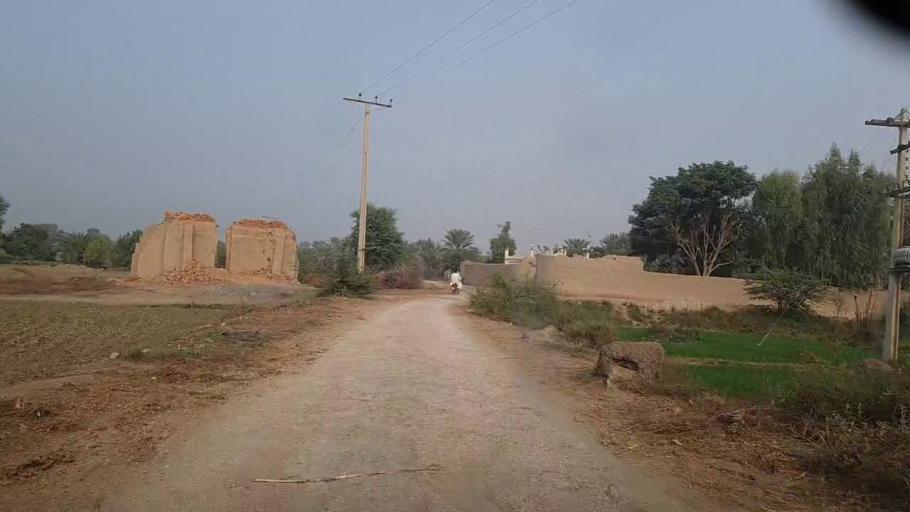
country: PK
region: Sindh
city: Bozdar
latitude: 27.1436
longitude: 68.6672
